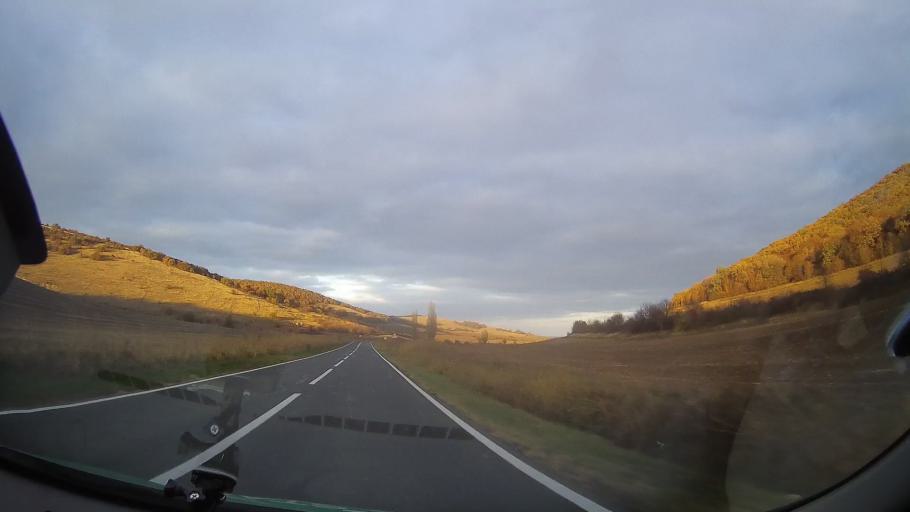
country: RO
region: Tulcea
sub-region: Comuna Ciucurova
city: Ciucurova
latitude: 44.9595
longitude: 28.5187
